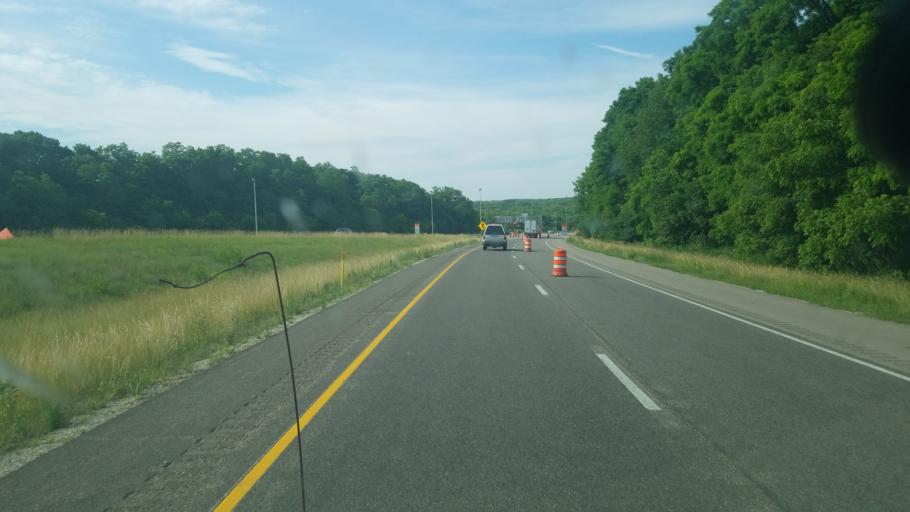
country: US
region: Illinois
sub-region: Peoria County
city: Bellevue
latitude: 40.7371
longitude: -89.6713
